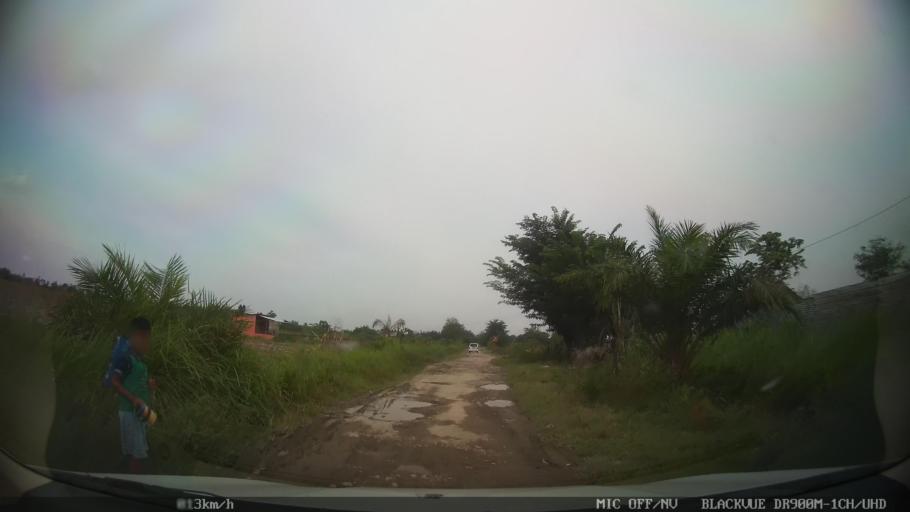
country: ID
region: North Sumatra
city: Medan
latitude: 3.5734
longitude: 98.7438
